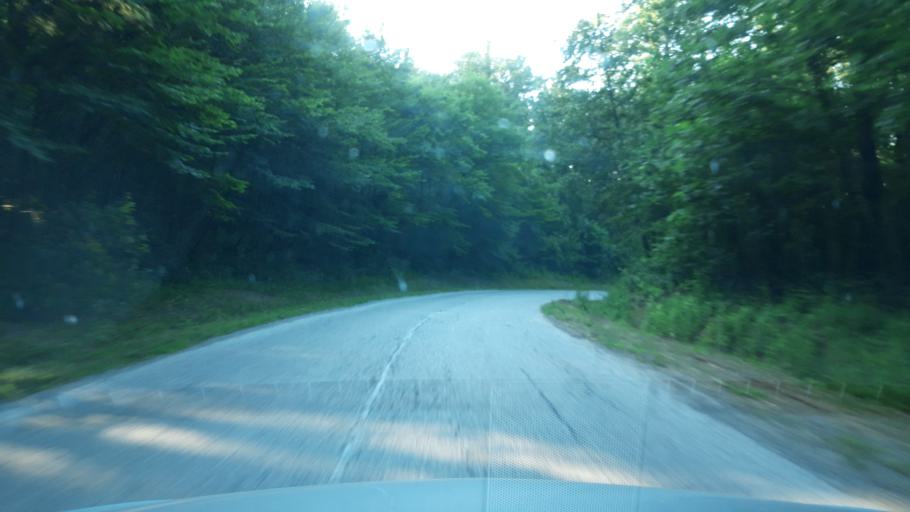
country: RS
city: Glozan
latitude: 45.1582
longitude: 19.5867
